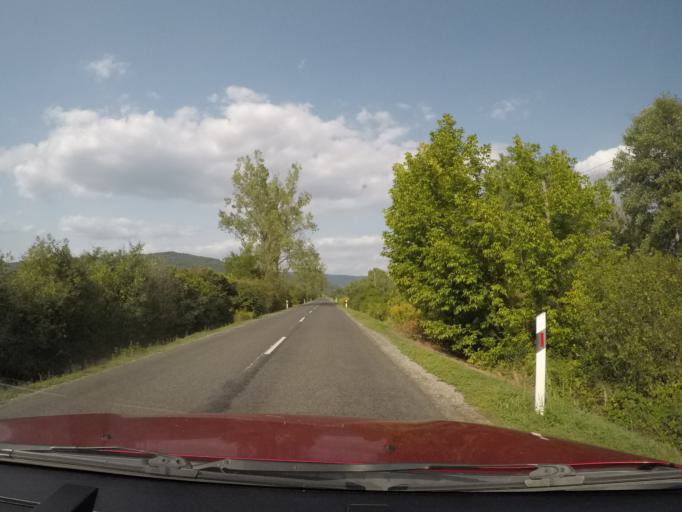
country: HU
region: Borsod-Abauj-Zemplen
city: Szendro
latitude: 48.5061
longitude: 20.7018
